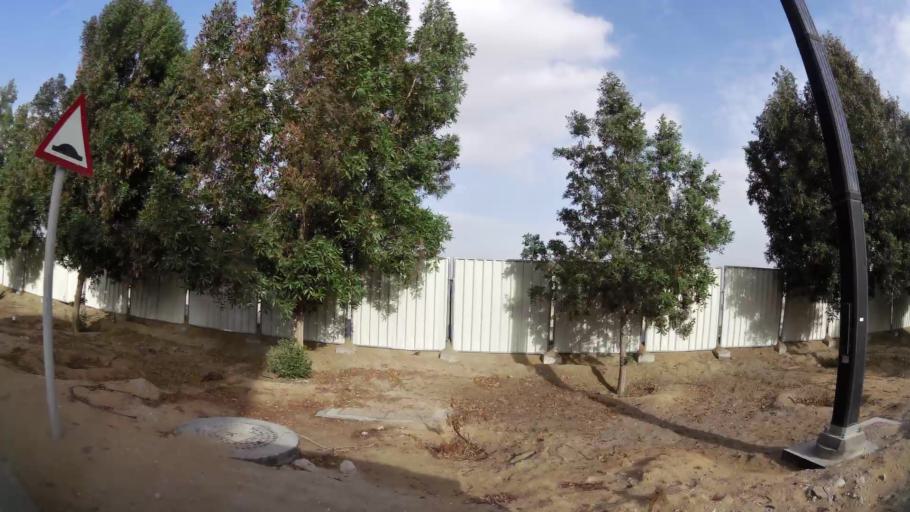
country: AE
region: Abu Dhabi
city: Abu Dhabi
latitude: 24.5064
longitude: 54.6024
